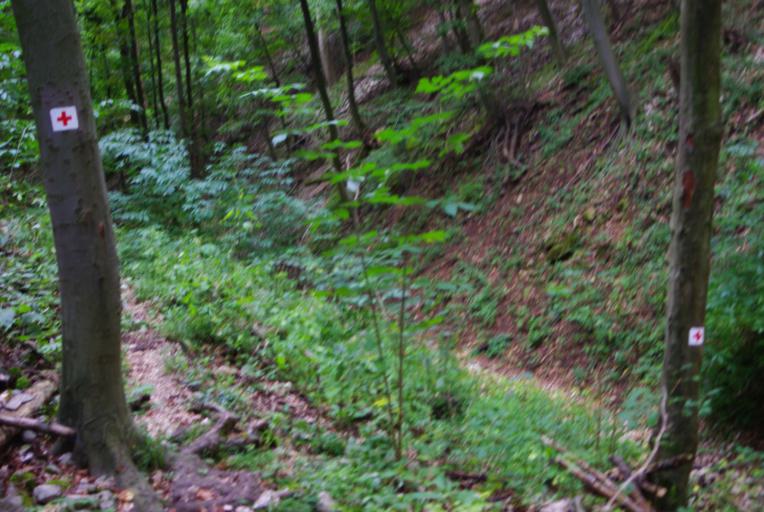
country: HU
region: Pest
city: Pilisszentkereszt
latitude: 47.7050
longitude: 18.8675
